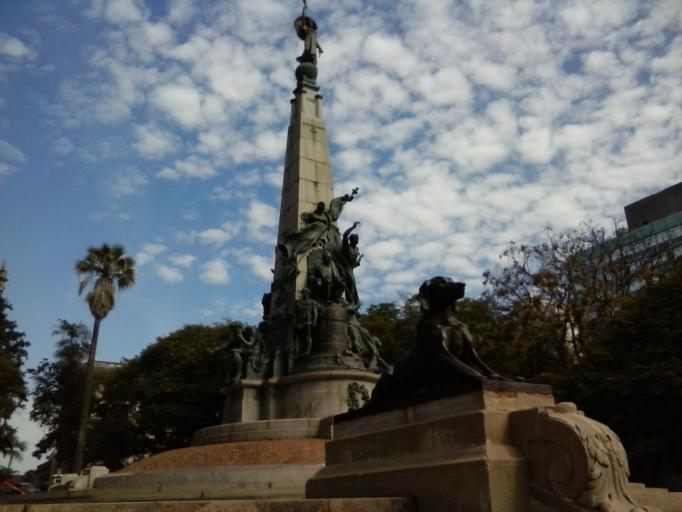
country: BR
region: Rio Grande do Sul
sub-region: Porto Alegre
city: Porto Alegre
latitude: -30.0325
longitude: -51.2301
